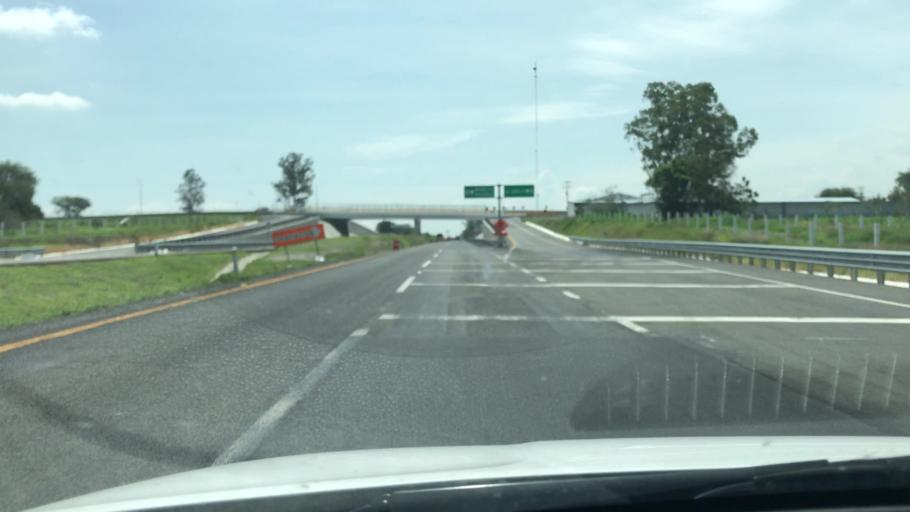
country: MX
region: Jalisco
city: La Barca
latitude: 20.3229
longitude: -102.5701
